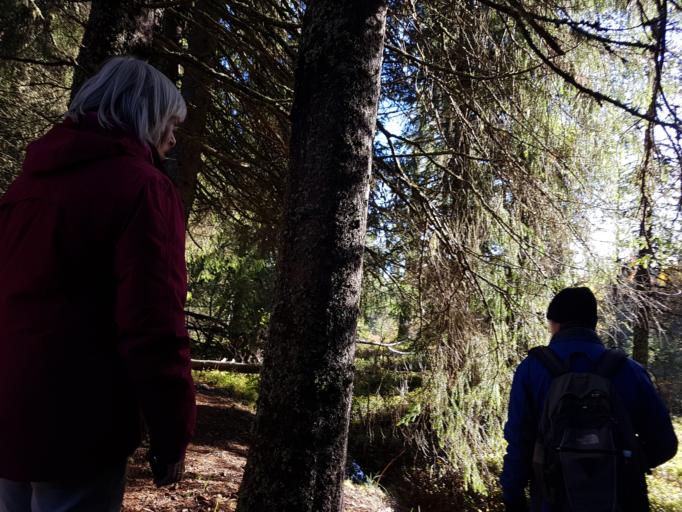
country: NO
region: Sor-Trondelag
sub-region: Trondheim
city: Trondheim
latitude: 63.4224
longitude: 10.2958
